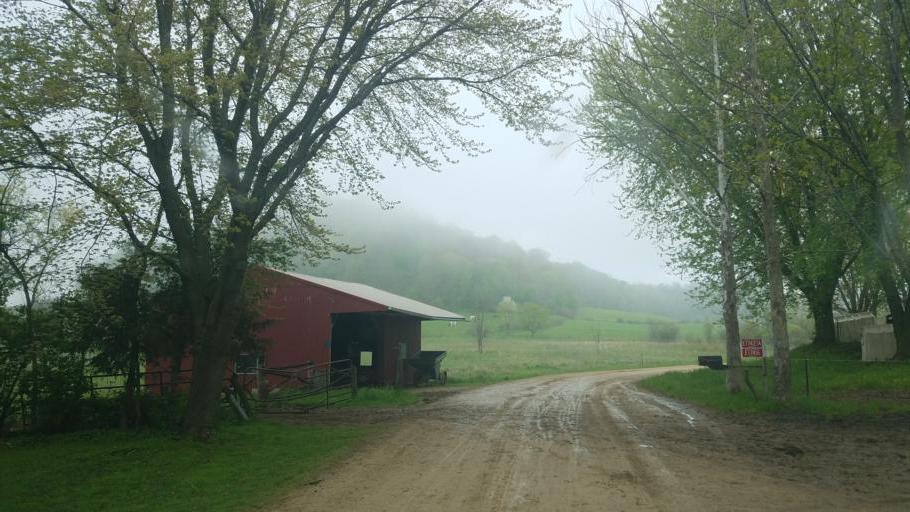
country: US
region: Wisconsin
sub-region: Vernon County
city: Hillsboro
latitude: 43.6224
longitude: -90.3859
